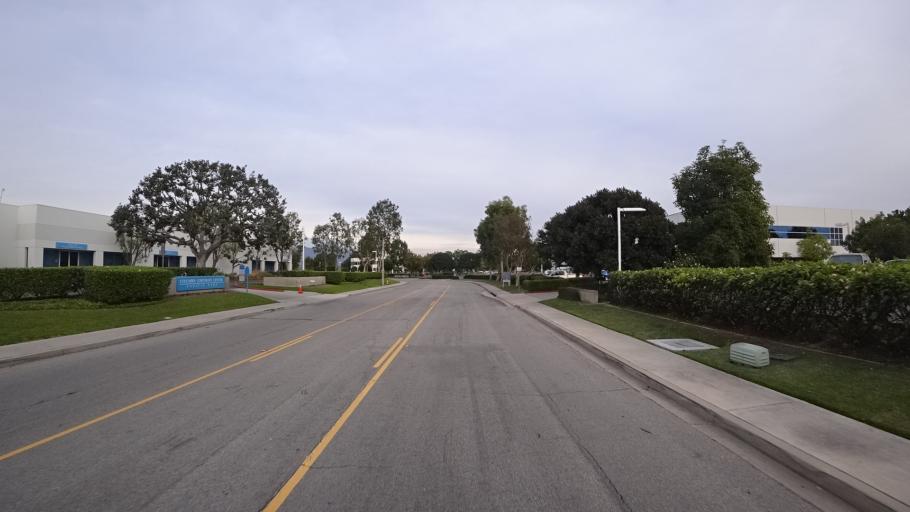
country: US
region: California
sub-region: Orange County
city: Laguna Woods
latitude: 33.5877
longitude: -117.7245
